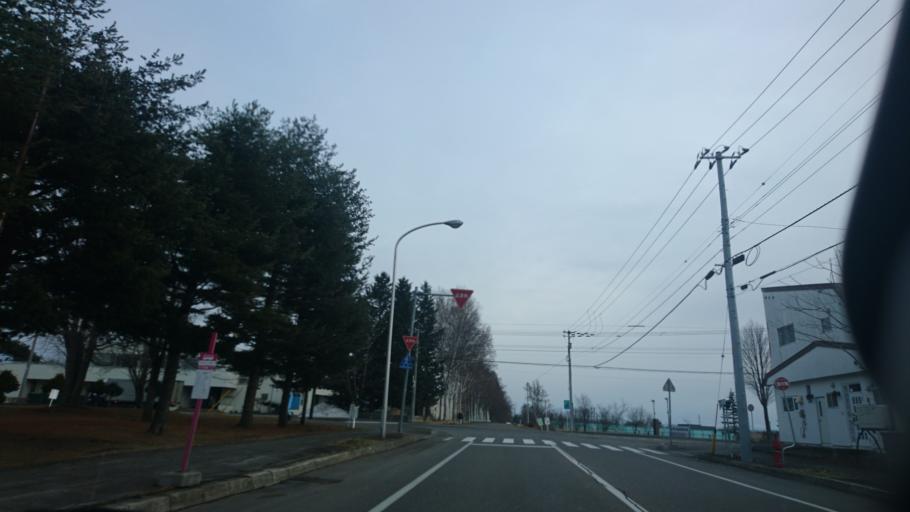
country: JP
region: Hokkaido
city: Otofuke
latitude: 42.9920
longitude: 143.1926
